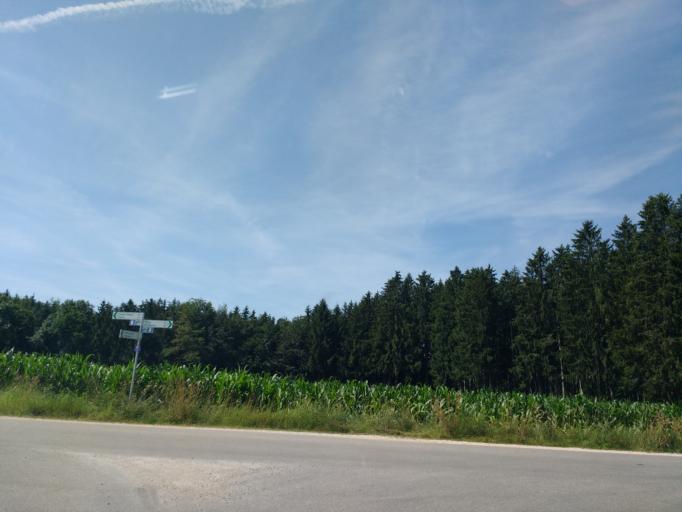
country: DE
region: Bavaria
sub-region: Upper Bavaria
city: Seeon-Seebruck
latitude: 47.9910
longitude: 12.4480
